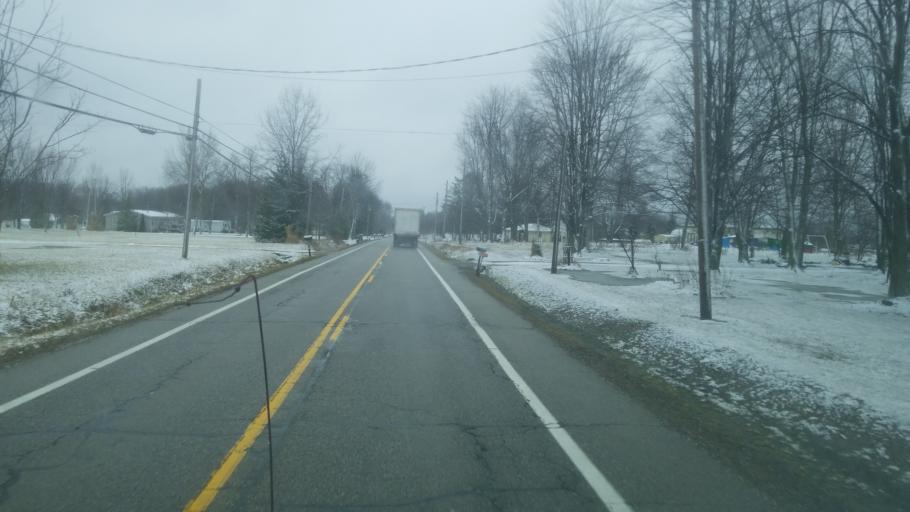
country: US
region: Ohio
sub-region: Portage County
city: Garrettsville
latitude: 41.2439
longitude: -81.1272
